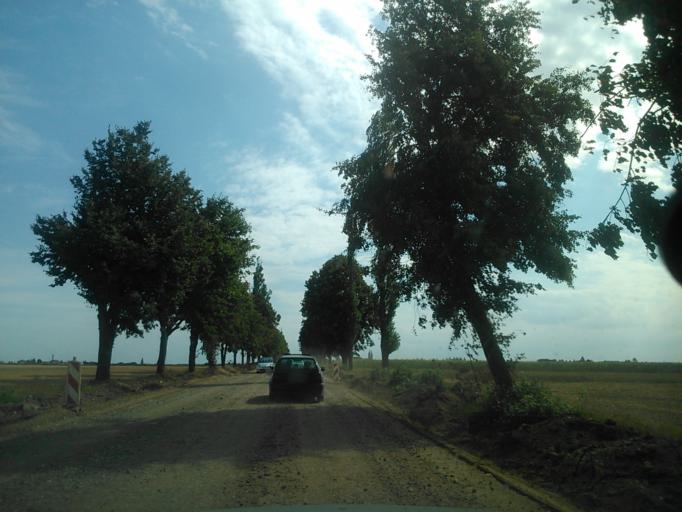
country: PL
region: Warmian-Masurian Voivodeship
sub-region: Powiat dzialdowski
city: Ilowo -Osada
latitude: 53.1843
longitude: 20.2876
